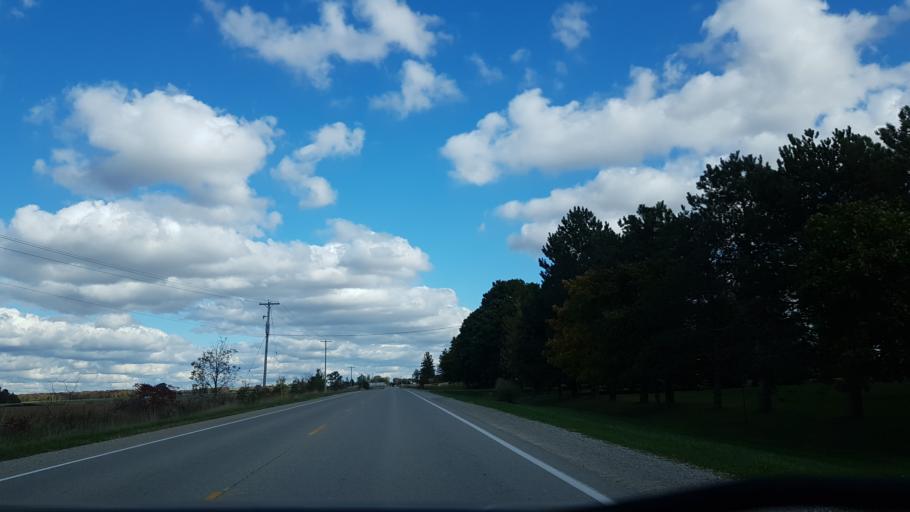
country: CA
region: Ontario
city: Lambton Shores
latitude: 43.2407
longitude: -81.7356
